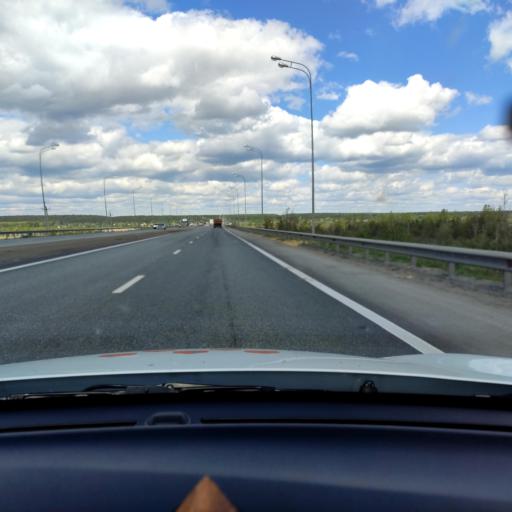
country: RU
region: Tatarstan
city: Osinovo
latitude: 55.8047
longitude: 48.8419
